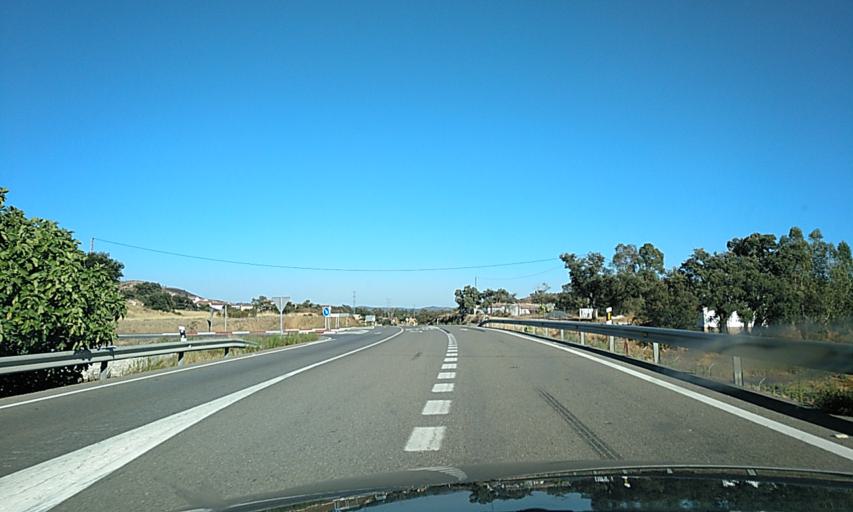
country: ES
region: Andalusia
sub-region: Provincia de Huelva
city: Santa Barbara de Casa
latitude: 37.7943
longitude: -7.1940
